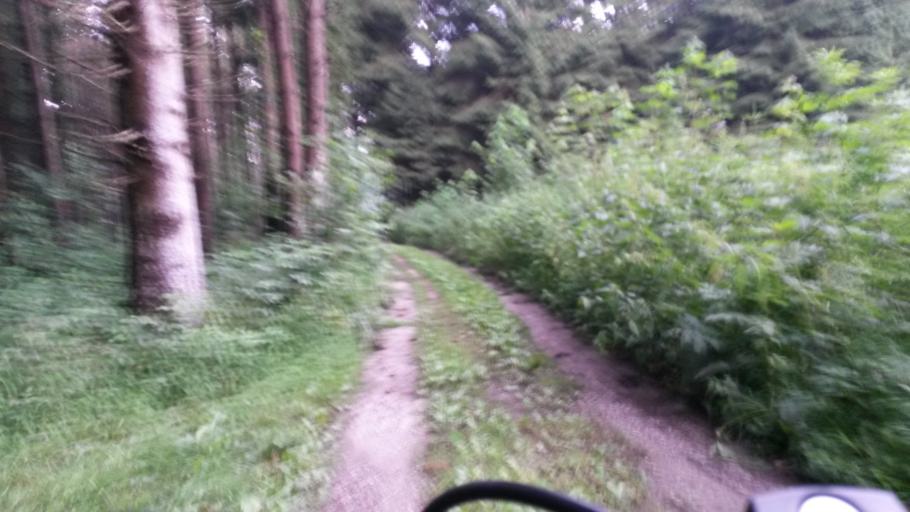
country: DE
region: Bavaria
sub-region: Upper Bavaria
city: Hoslwang
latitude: 47.9665
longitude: 12.3088
